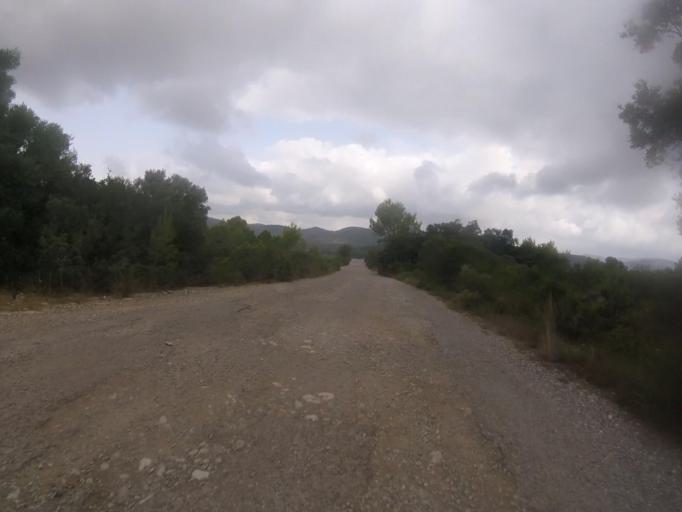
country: ES
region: Valencia
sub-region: Provincia de Castello
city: Santa Magdalena de Pulpis
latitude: 40.3405
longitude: 0.2740
